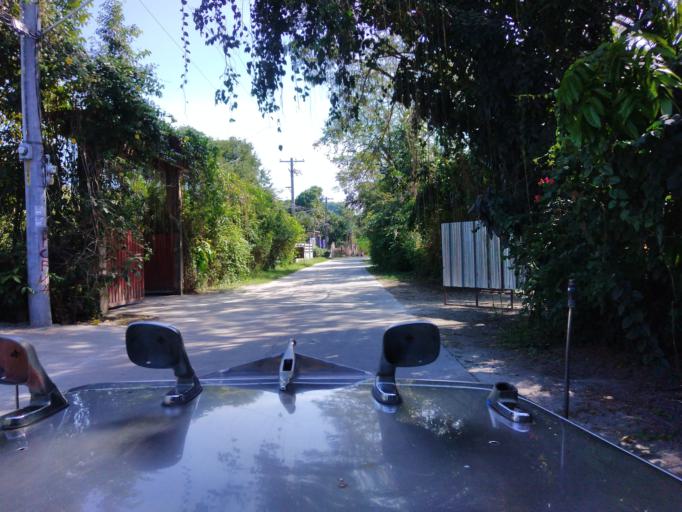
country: PH
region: Central Luzon
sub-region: Province of Pampanga
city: Bacolor
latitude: 15.0061
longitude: 120.6651
